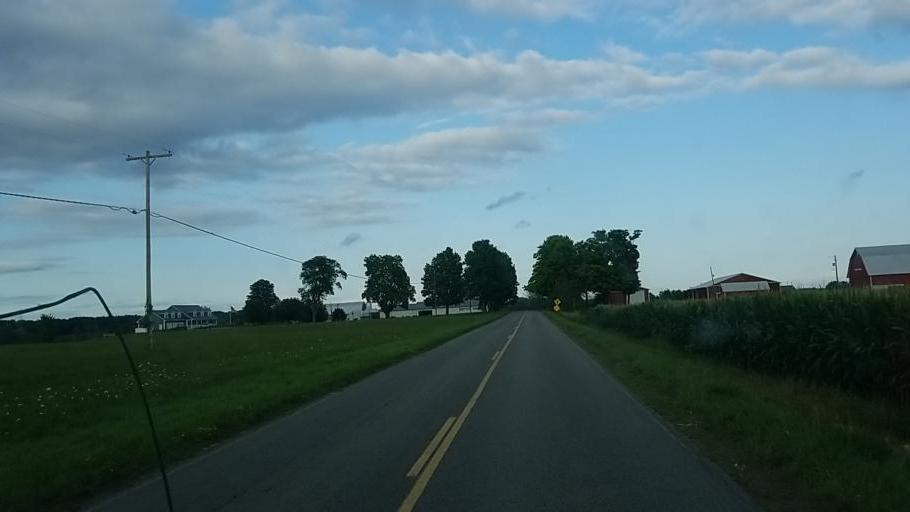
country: US
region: Michigan
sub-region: Montcalm County
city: Lakeview
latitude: 43.3375
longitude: -85.3472
